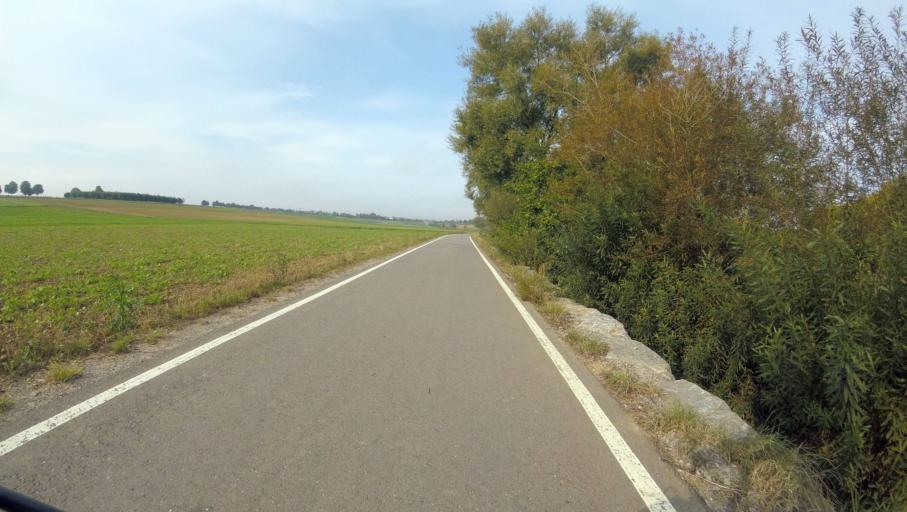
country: DE
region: Baden-Wuerttemberg
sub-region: Regierungsbezirk Stuttgart
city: Bondorf
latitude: 48.5295
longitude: 8.8583
